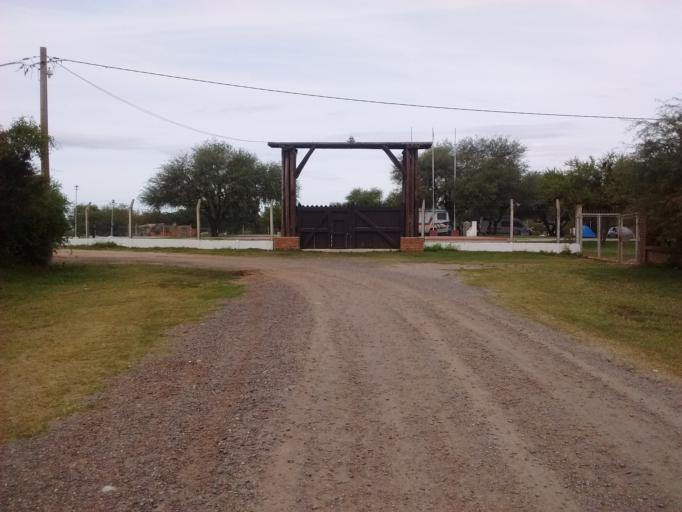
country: AR
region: Santa Fe
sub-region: Departamento de San Lorenzo
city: San Lorenzo
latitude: -32.4439
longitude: -60.8099
